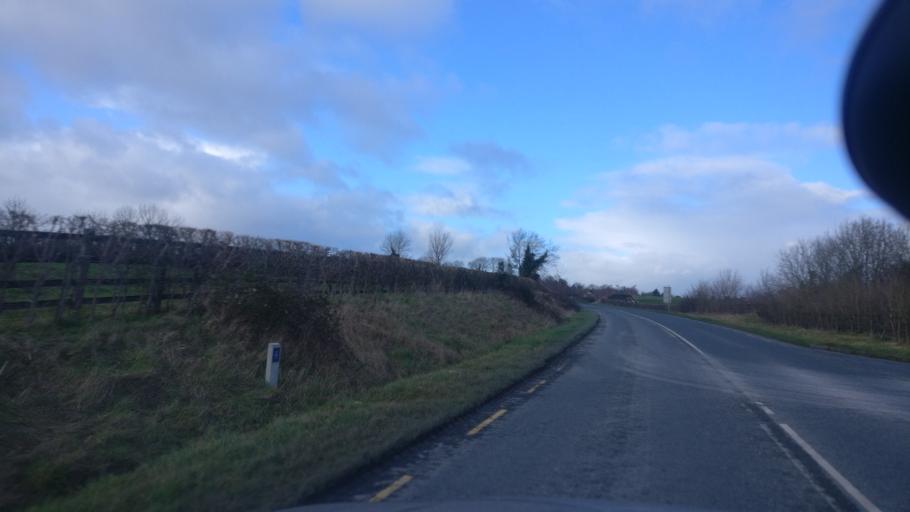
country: IE
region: Leinster
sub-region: Kilkenny
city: Kilkenny
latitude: 52.6041
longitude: -7.1937
